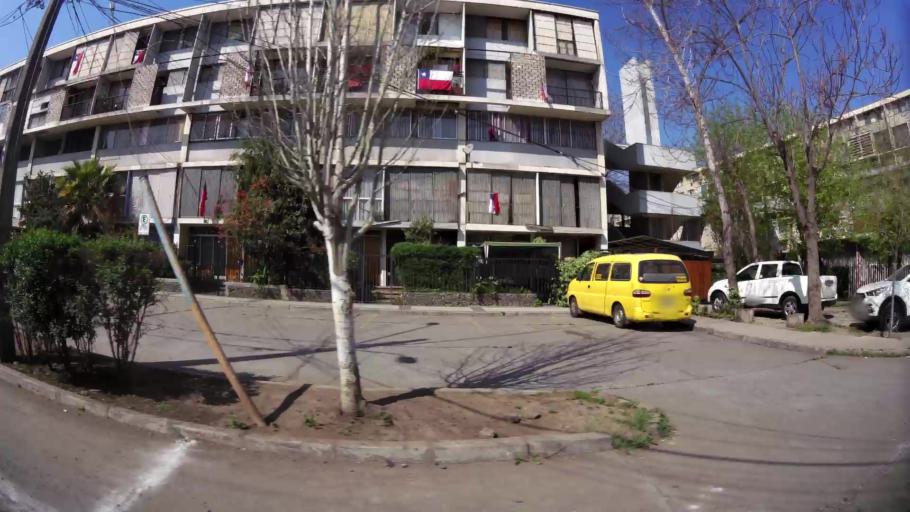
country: CL
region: Santiago Metropolitan
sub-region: Provincia de Santiago
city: Lo Prado
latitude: -33.4486
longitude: -70.6902
